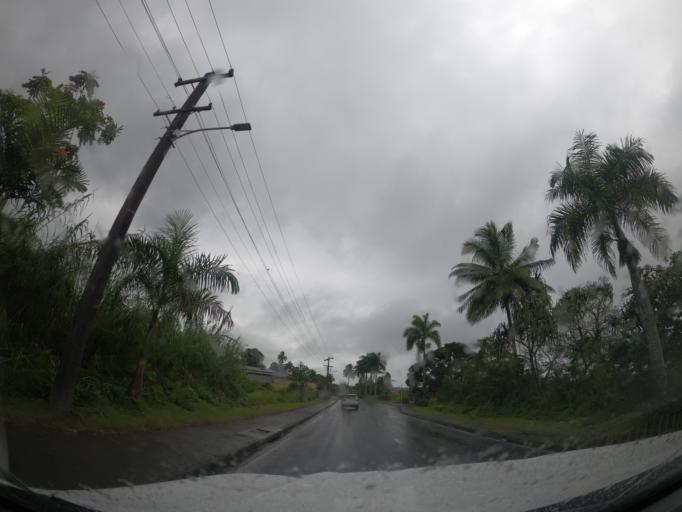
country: FJ
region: Central
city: Suva
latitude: -18.1133
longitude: 178.4196
